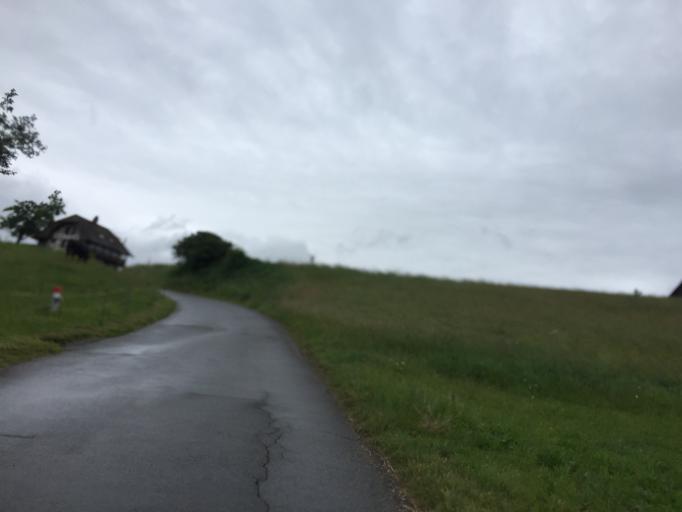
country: CH
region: Bern
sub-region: Bern-Mittelland District
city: Biglen
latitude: 46.9115
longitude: 7.6020
